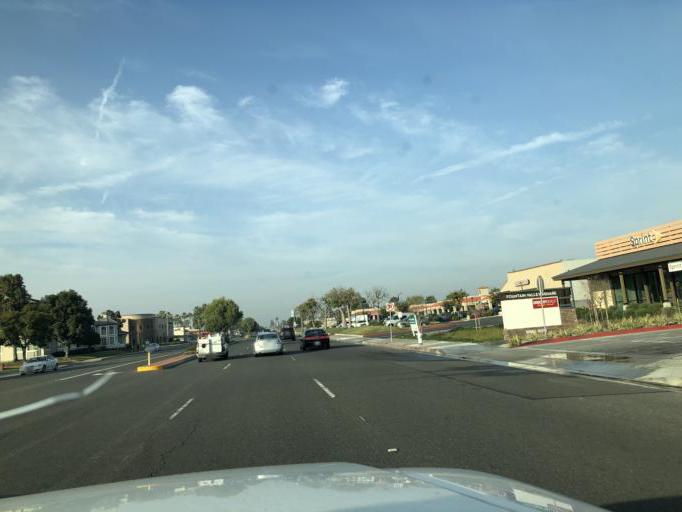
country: US
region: California
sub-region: Orange County
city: Fountain Valley
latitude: 33.6884
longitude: -117.9544
